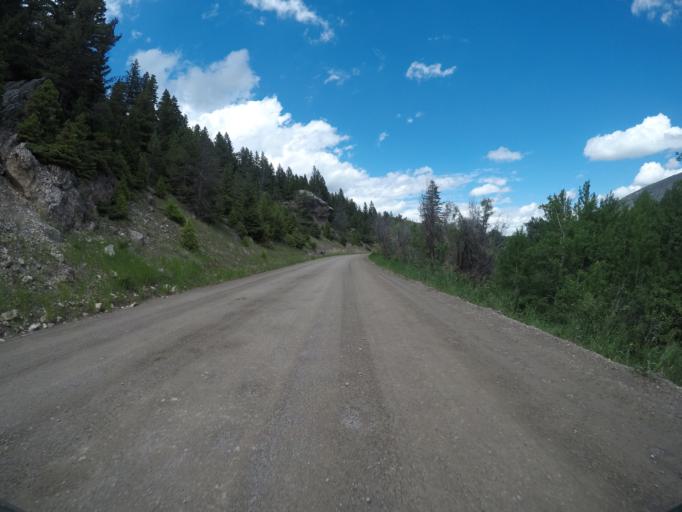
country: US
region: Montana
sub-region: Park County
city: Livingston
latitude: 45.5419
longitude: -110.2156
